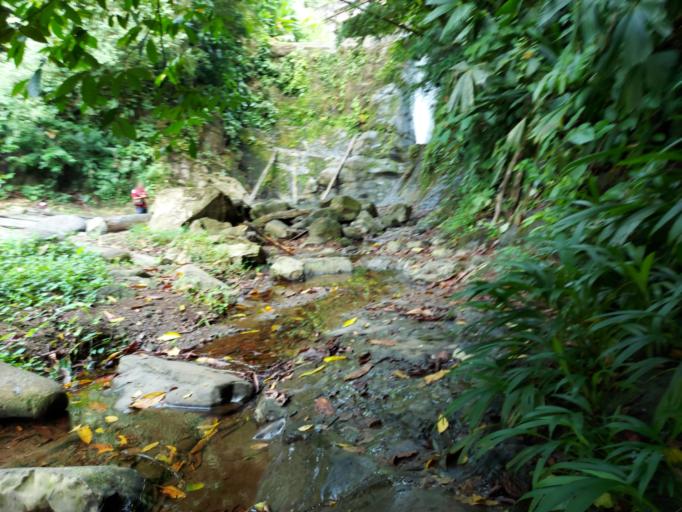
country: PA
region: Bocas del Toro
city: Barranco
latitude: 9.6316
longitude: -82.8191
